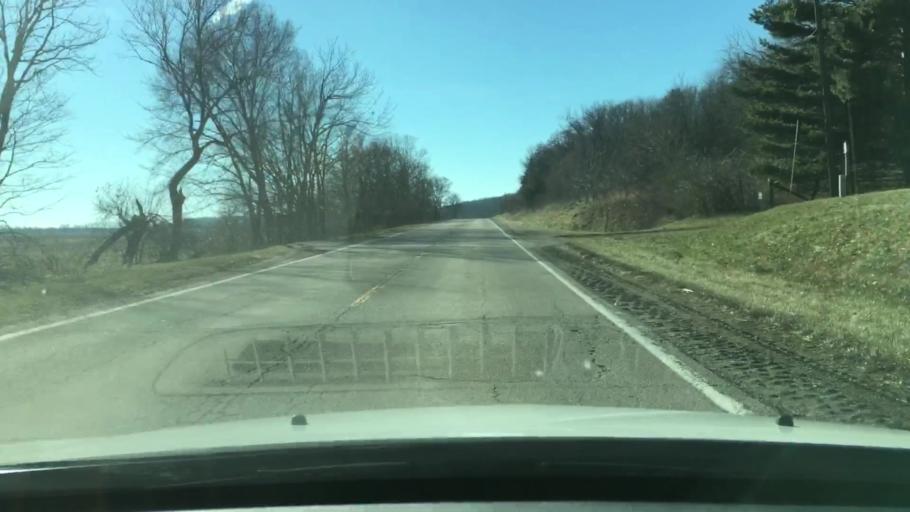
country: US
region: Illinois
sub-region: Mason County
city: Havana
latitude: 40.2525
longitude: -90.1824
